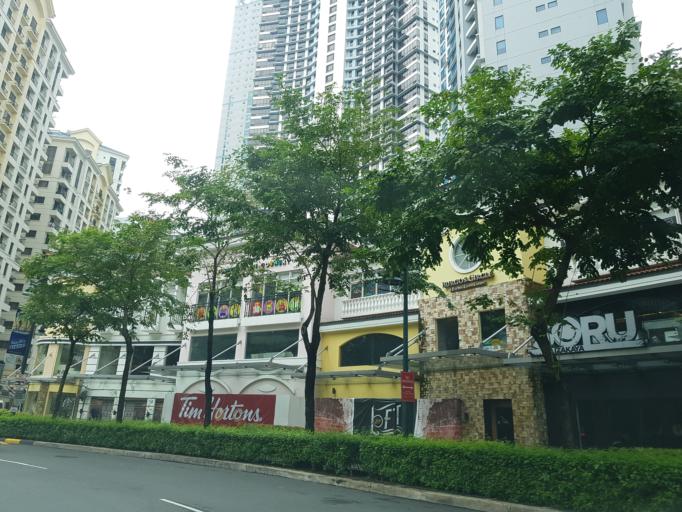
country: PH
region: Metro Manila
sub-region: Makati City
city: Makati City
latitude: 14.5526
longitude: 121.0441
